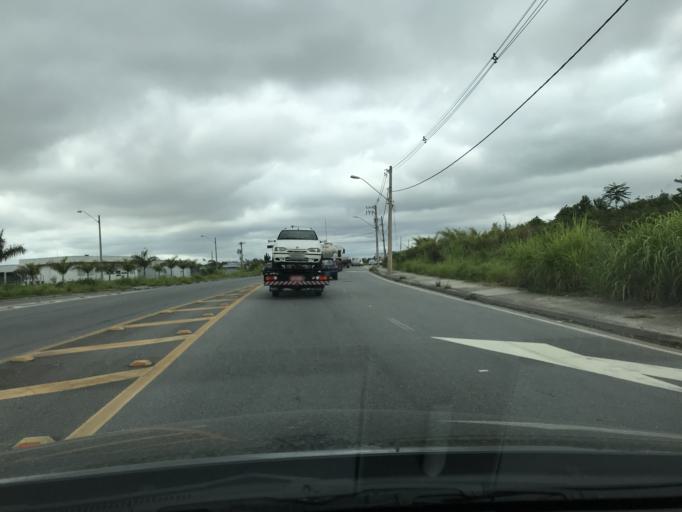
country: BR
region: Sao Paulo
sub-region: Itaquaquecetuba
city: Itaquaquecetuba
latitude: -23.4775
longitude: -46.3268
